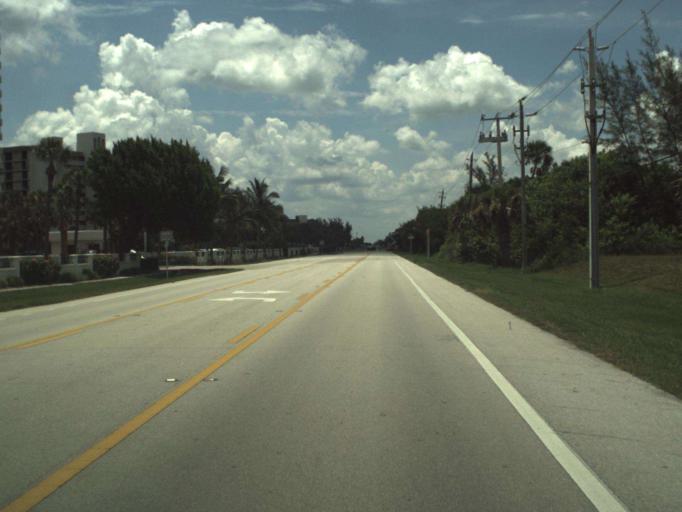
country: US
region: Florida
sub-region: Saint Lucie County
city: Hutchinson Island South
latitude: 27.2837
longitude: -80.2112
